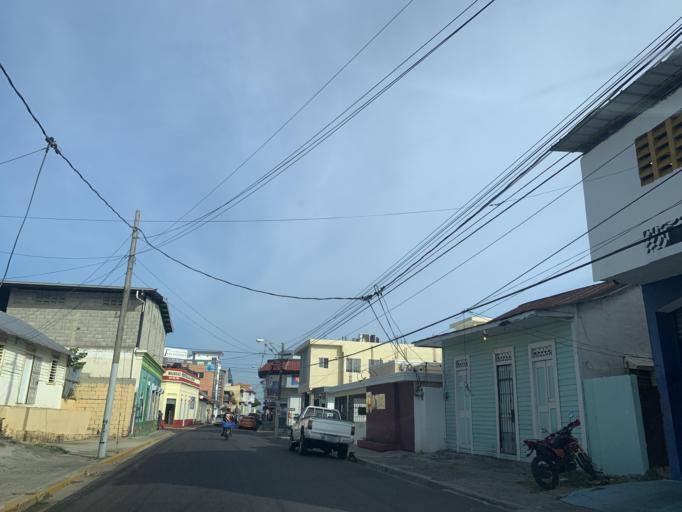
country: DO
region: Puerto Plata
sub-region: Puerto Plata
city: Puerto Plata
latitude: 19.7960
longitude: -70.6872
